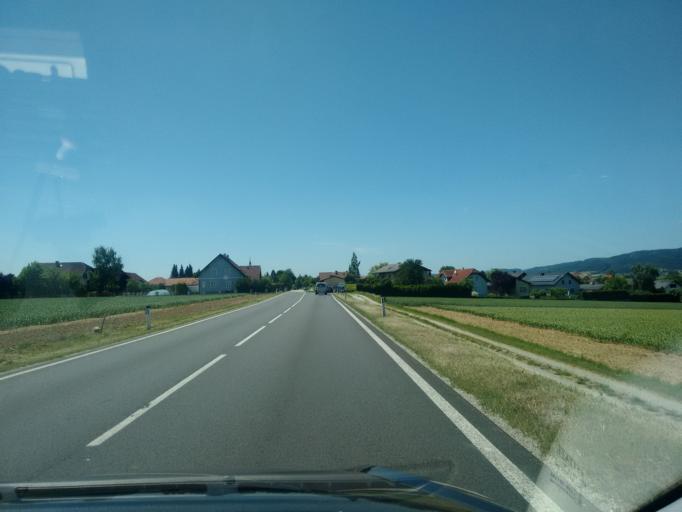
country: AT
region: Lower Austria
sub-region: Politischer Bezirk Sankt Polten
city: Gerersdorf
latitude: 48.1992
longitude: 15.5621
